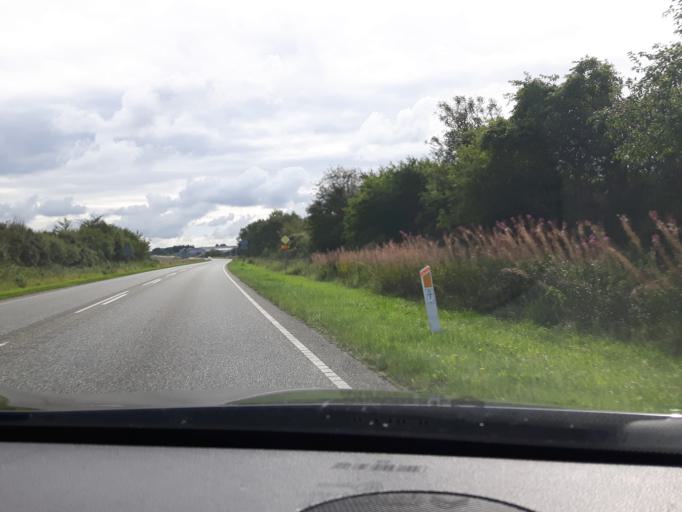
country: DK
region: South Denmark
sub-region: Vejle Kommune
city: Borkop
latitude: 55.6448
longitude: 9.6630
